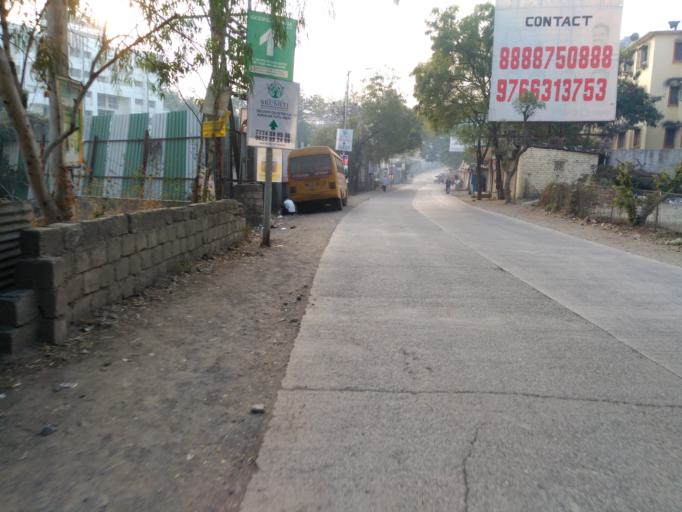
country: IN
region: Maharashtra
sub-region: Pune Division
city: Pune
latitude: 18.4540
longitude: 73.9144
